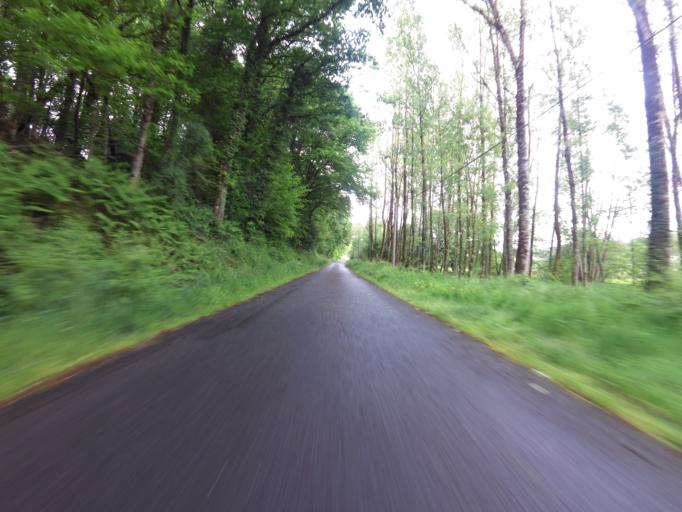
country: FR
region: Brittany
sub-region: Departement du Morbihan
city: Pluherlin
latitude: 47.7121
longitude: -2.3746
